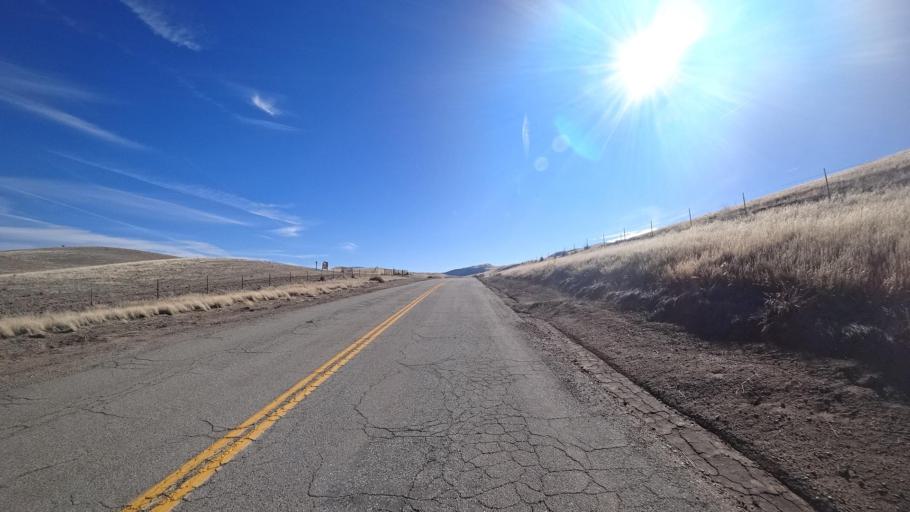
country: US
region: California
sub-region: Kern County
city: Maricopa
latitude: 34.9389
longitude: -119.4046
